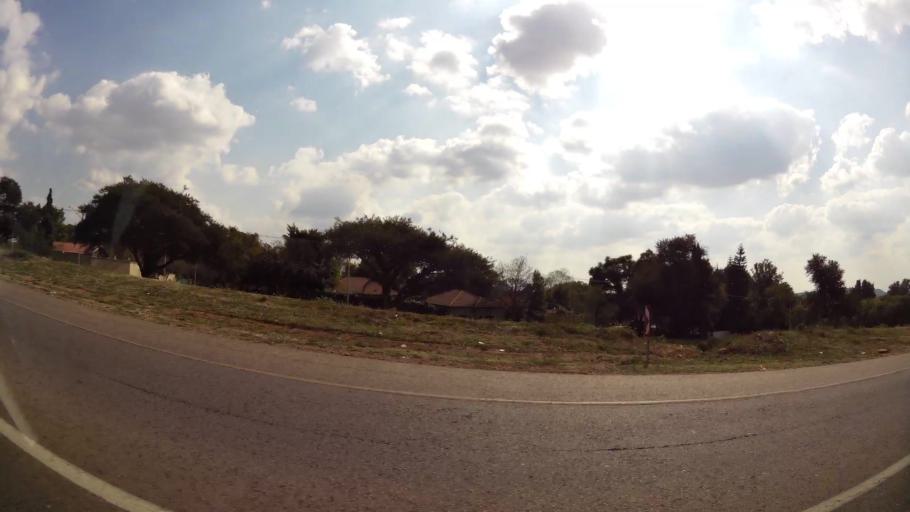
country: ZA
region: Gauteng
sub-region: City of Tshwane Metropolitan Municipality
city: Centurion
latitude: -25.8065
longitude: 28.2920
